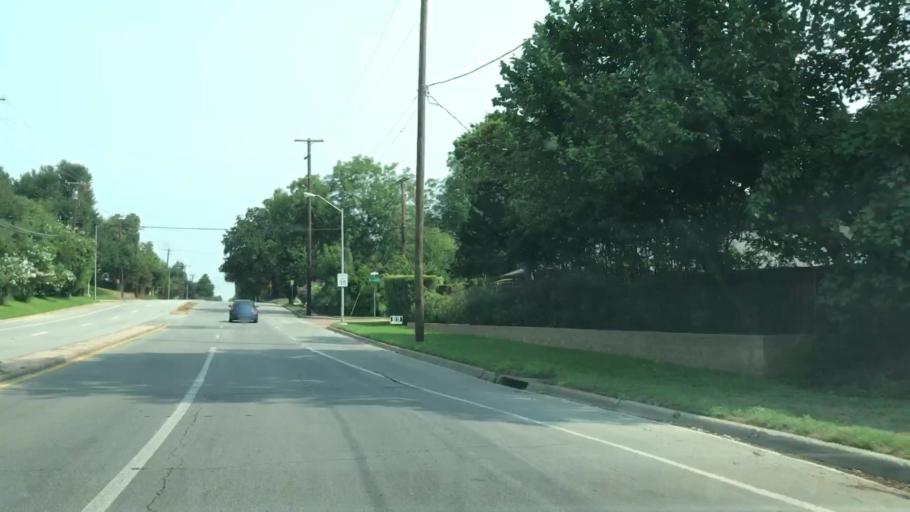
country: US
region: Texas
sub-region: Dallas County
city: Dallas
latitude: 32.7592
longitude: -96.8355
